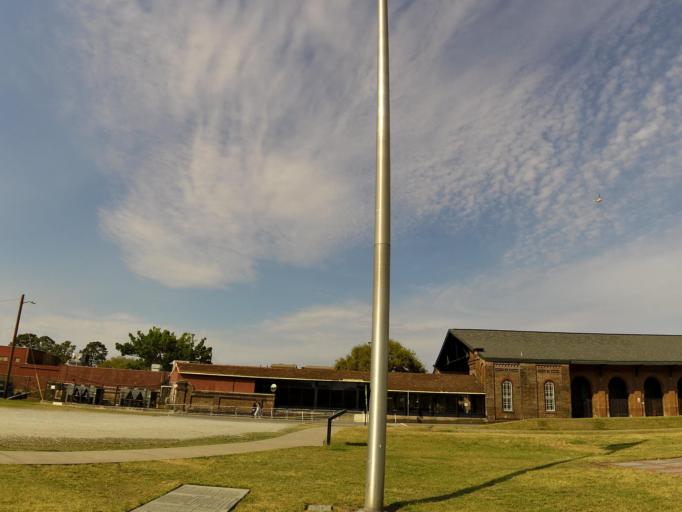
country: US
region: Florida
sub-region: Franklin County
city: Carrabelle
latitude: 29.3178
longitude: -84.3895
